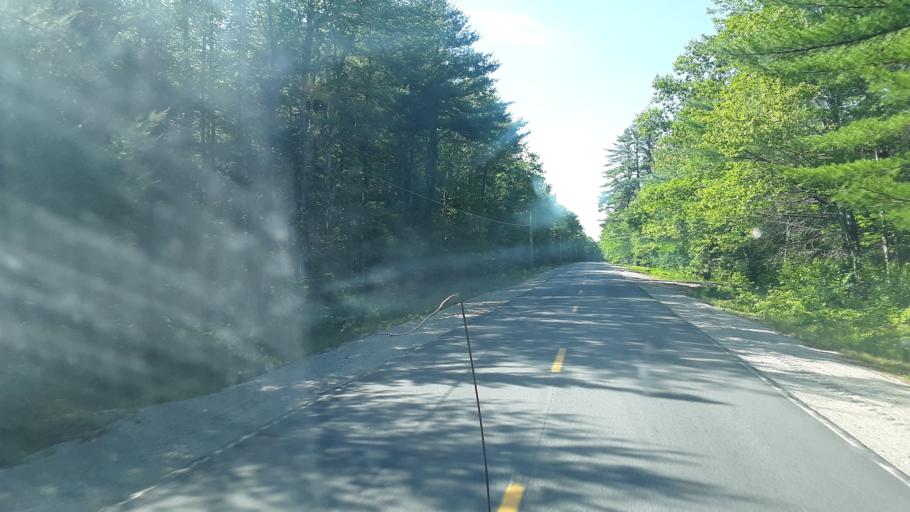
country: US
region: Maine
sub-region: Washington County
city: Cherryfield
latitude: 44.7685
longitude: -68.0294
